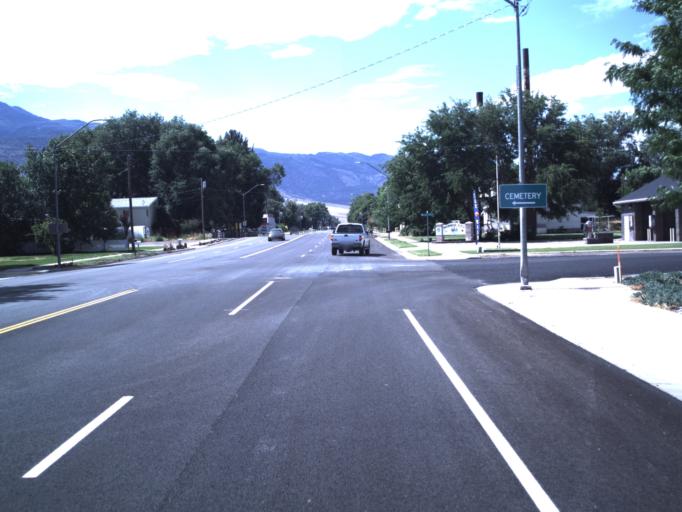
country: US
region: Utah
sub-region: Sevier County
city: Monroe
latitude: 38.6392
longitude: -112.1215
